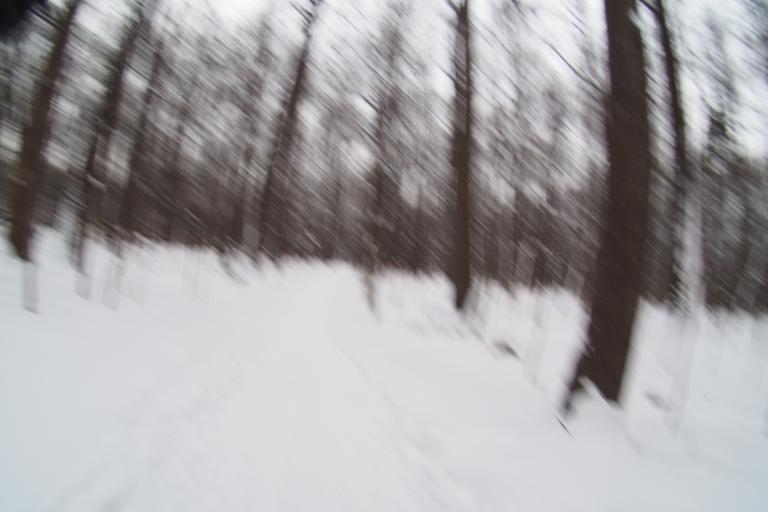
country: RU
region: Moskovskaya
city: Izmaylovo
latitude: 55.7747
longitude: 37.7875
